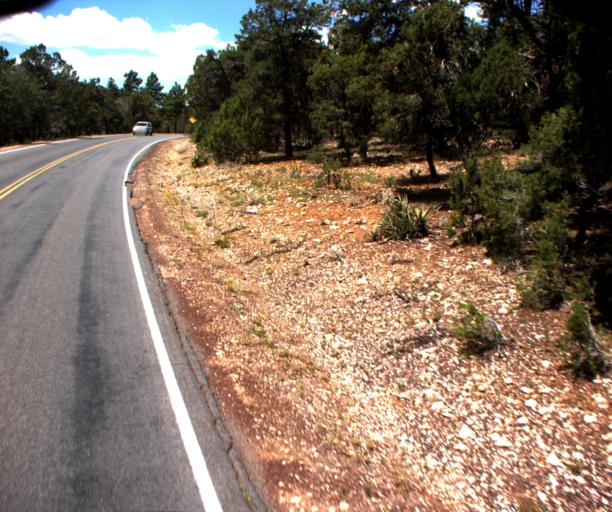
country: US
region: Arizona
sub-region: Coconino County
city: Grand Canyon
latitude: 36.0117
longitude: -112.0641
